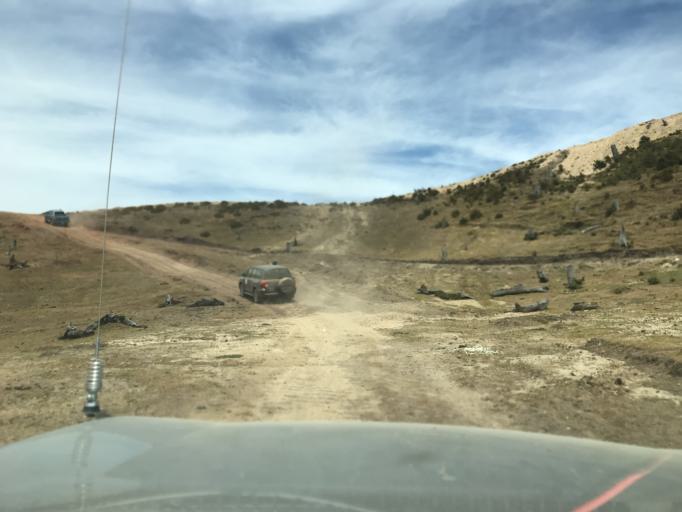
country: TL
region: Ainaro
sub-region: Ainaro
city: Ainaro
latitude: -8.8733
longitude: 125.5229
